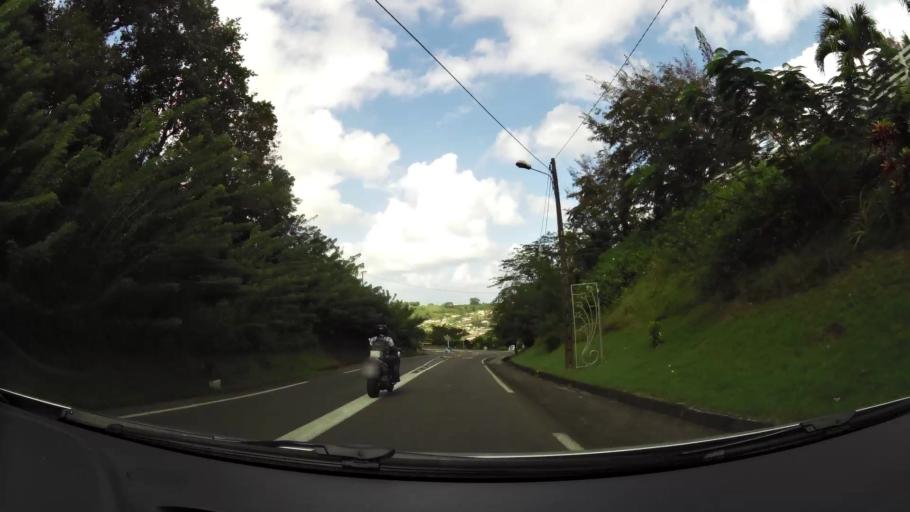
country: MQ
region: Martinique
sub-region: Martinique
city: Le Lorrain
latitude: 14.8185
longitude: -61.0269
